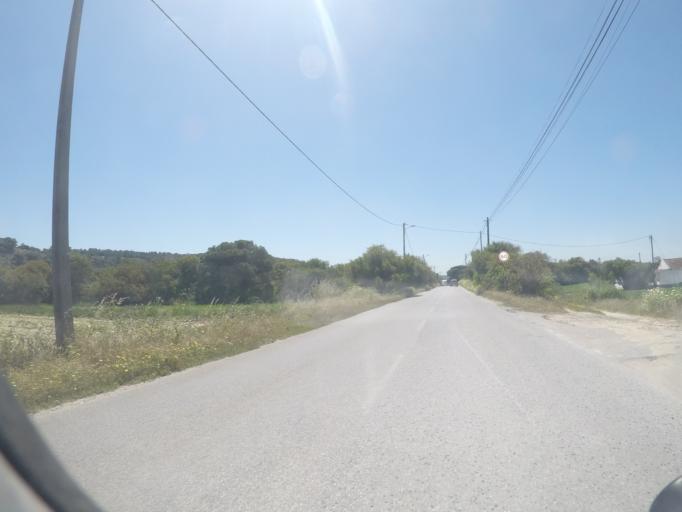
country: PT
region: Setubal
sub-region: Almada
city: Charneca
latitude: 38.6233
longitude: -9.2156
